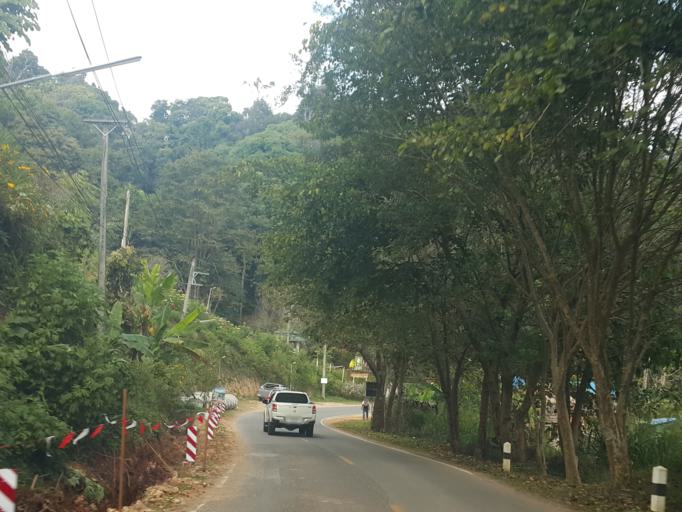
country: TH
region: Chiang Mai
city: Samoeng
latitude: 18.9252
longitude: 98.8225
